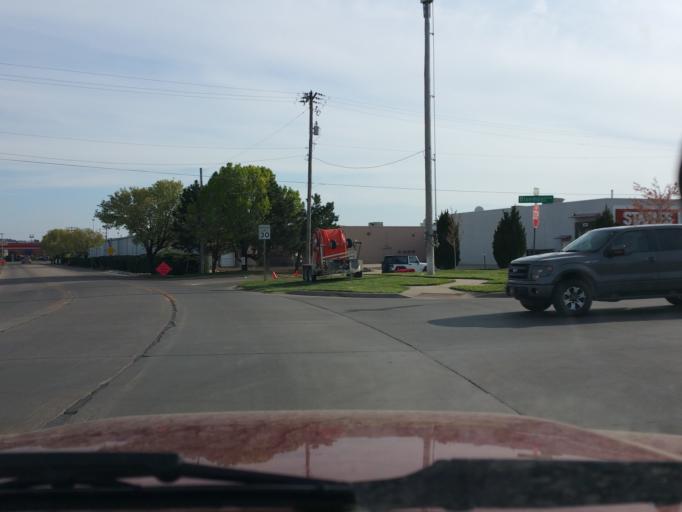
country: US
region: Kansas
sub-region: Riley County
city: Manhattan
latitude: 39.1861
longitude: -96.5556
